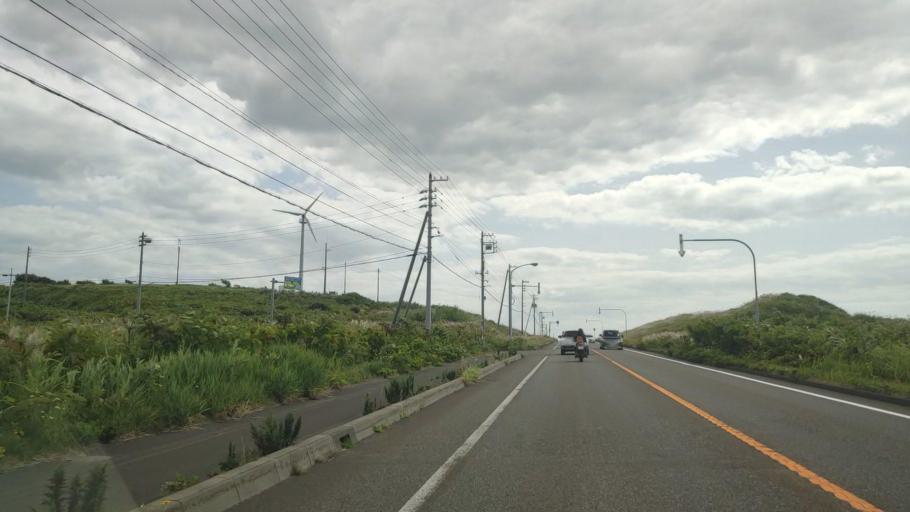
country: JP
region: Hokkaido
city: Rumoi
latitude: 44.5227
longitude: 141.7656
